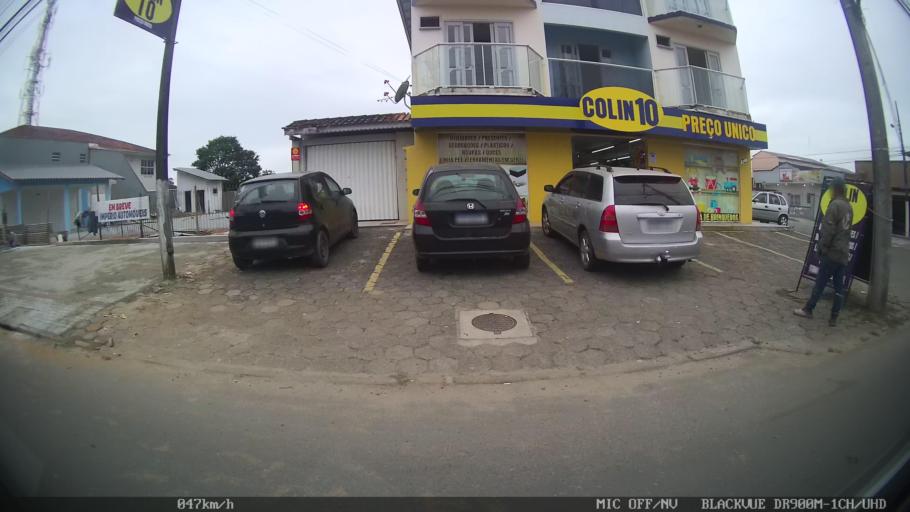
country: BR
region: Santa Catarina
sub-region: Joinville
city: Joinville
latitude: -26.3296
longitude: -48.8173
